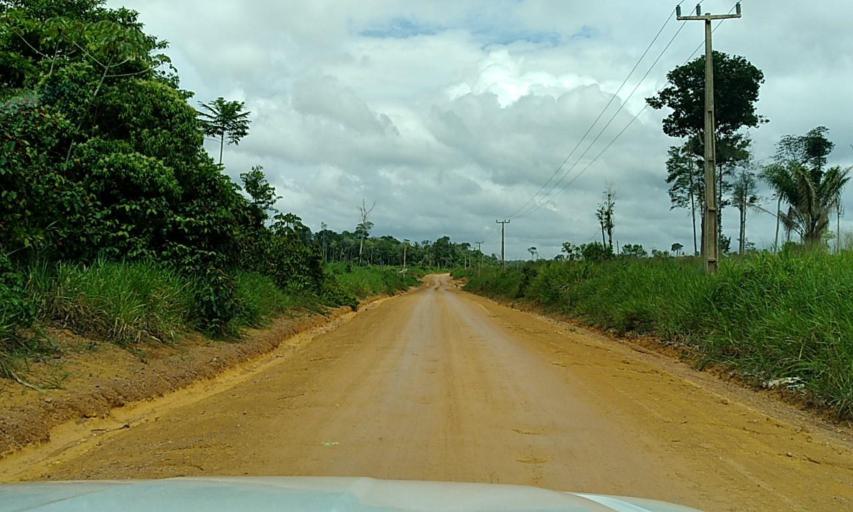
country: BR
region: Para
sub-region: Senador Jose Porfirio
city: Senador Jose Porfirio
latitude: -2.7823
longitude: -51.7722
